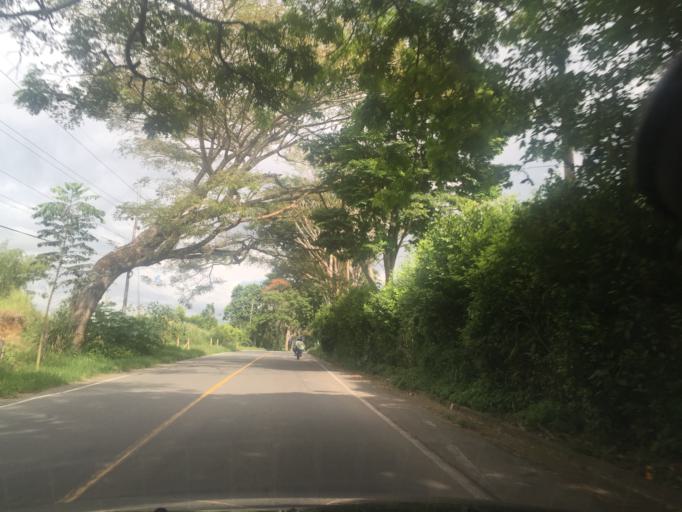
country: CO
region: Valle del Cauca
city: Caicedonia
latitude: 4.3417
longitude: -75.8368
